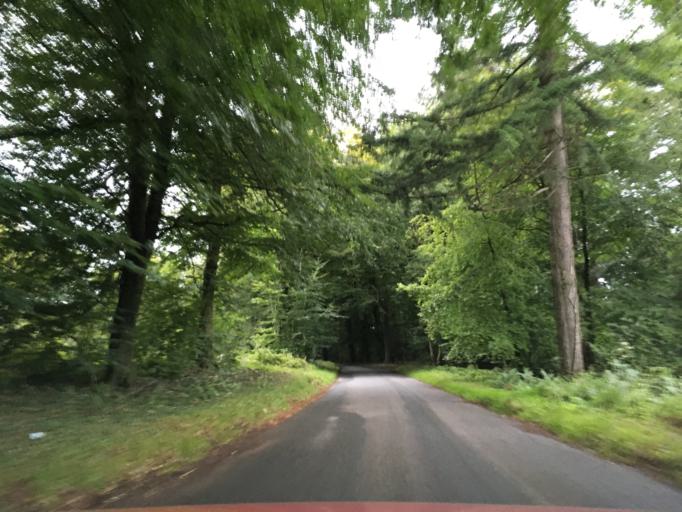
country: GB
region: Wales
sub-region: Newport
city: Llanvaches
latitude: 51.6498
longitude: -2.8377
